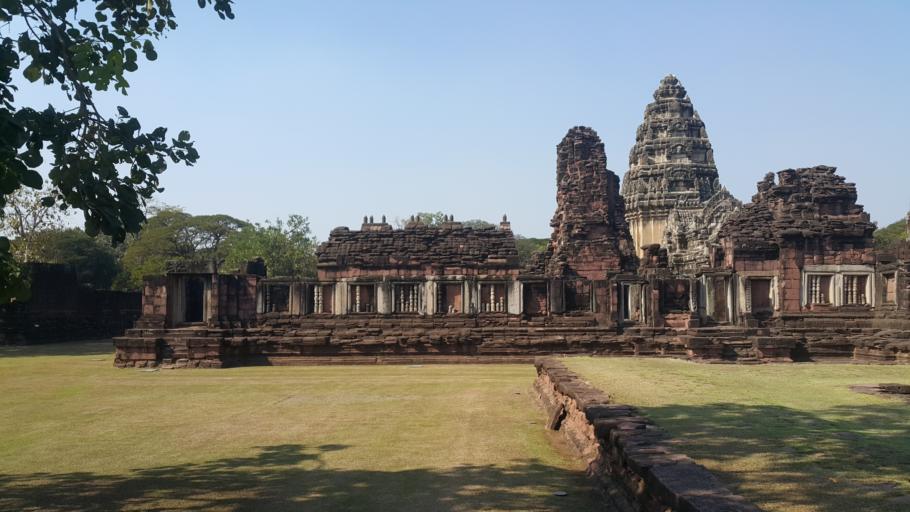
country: TH
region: Nakhon Ratchasima
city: Phimai
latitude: 15.2203
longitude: 102.4939
